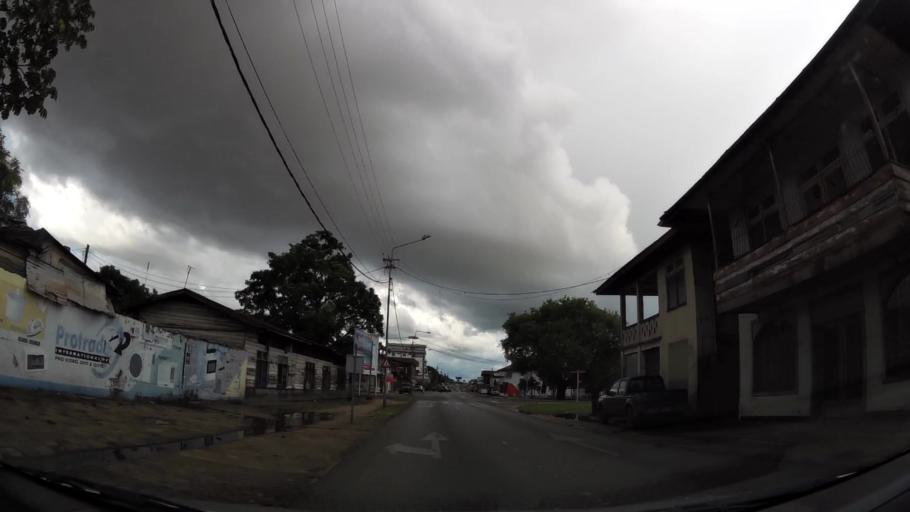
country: SR
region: Paramaribo
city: Paramaribo
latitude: 5.8343
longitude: -55.1661
